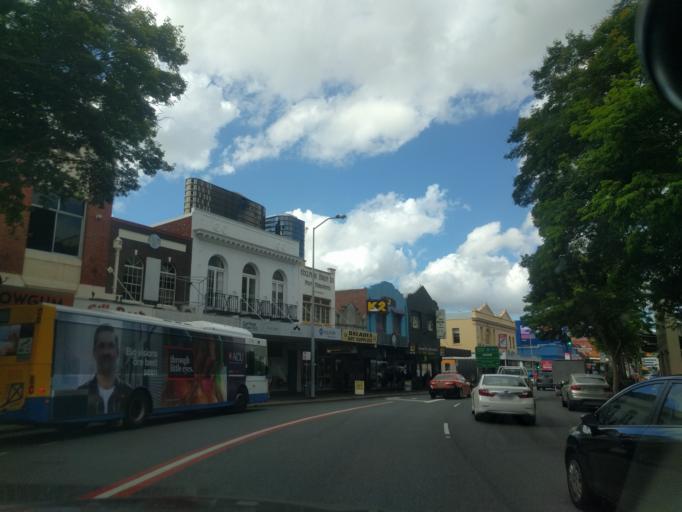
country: AU
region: Queensland
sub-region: Brisbane
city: Fortitude Valley
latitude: -27.4595
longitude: 153.0318
